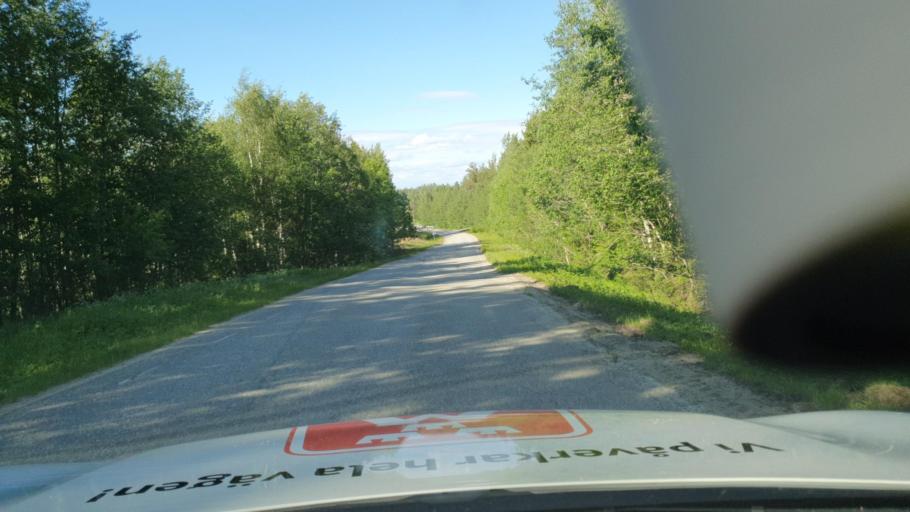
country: SE
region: Vaesterbotten
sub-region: Vannas Kommun
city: Vaennaes
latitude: 63.8471
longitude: 19.6221
